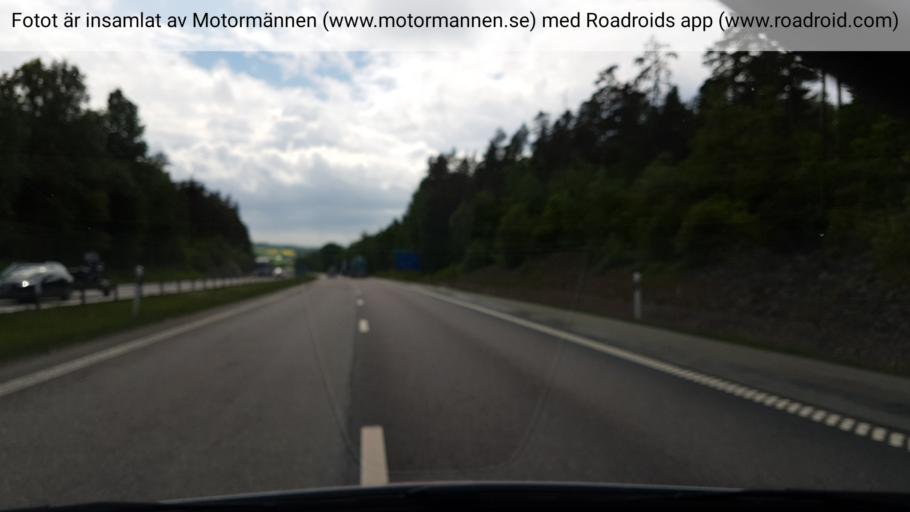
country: SE
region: Joenkoeping
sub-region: Jonkopings Kommun
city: Graenna
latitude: 58.0140
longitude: 14.4698
